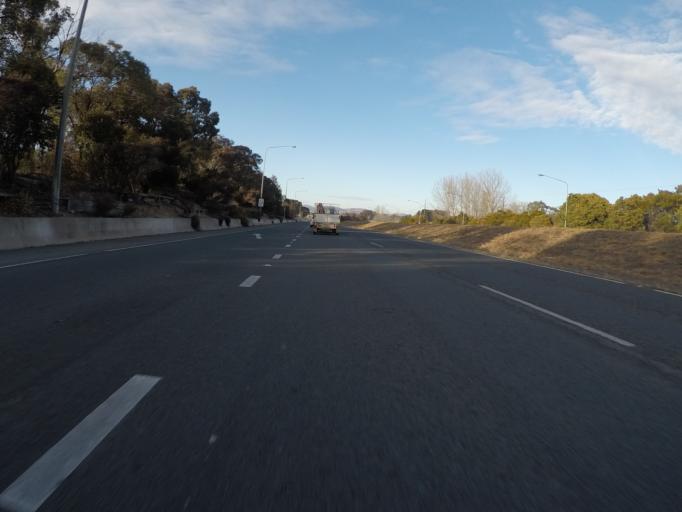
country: AU
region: Australian Capital Territory
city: Forrest
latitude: -35.3347
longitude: 149.1621
